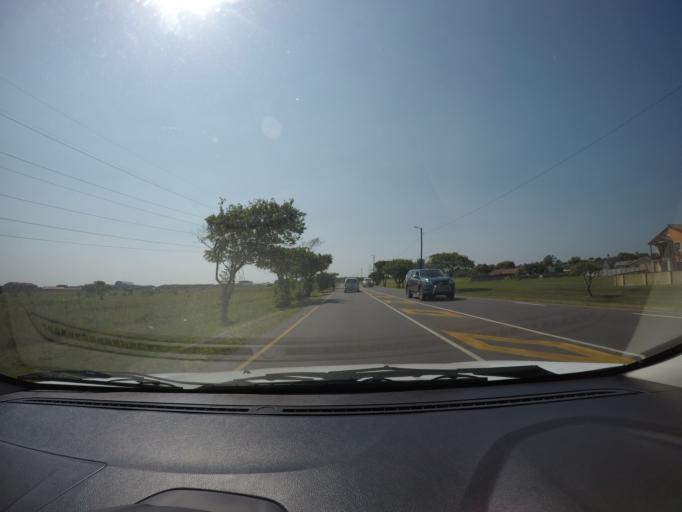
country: ZA
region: KwaZulu-Natal
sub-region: uThungulu District Municipality
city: Richards Bay
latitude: -28.7377
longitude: 32.0441
